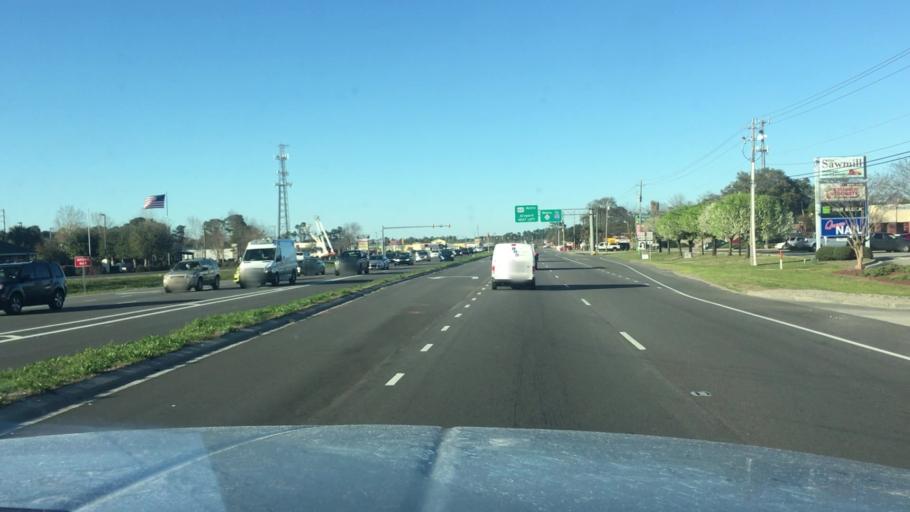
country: US
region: North Carolina
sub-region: New Hanover County
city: Myrtle Grove
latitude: 34.1352
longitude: -77.8947
